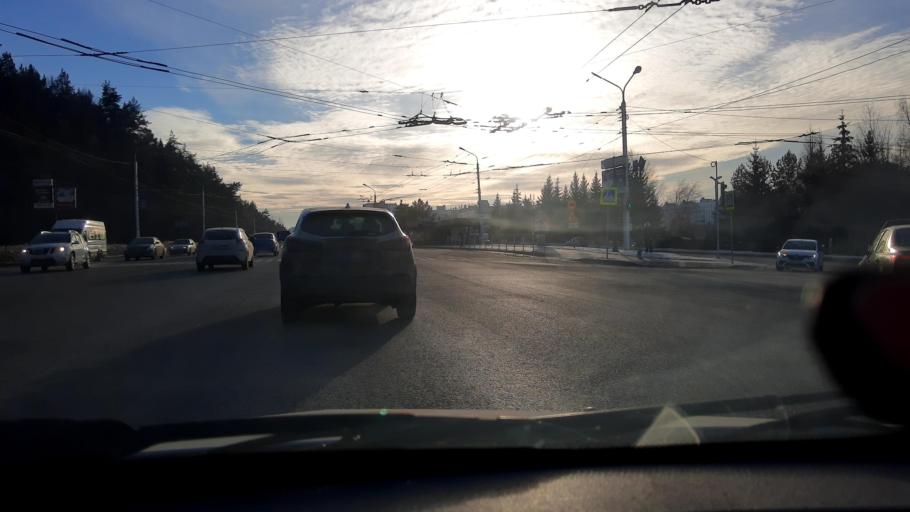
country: RU
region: Bashkortostan
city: Ufa
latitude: 54.7435
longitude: 56.0306
